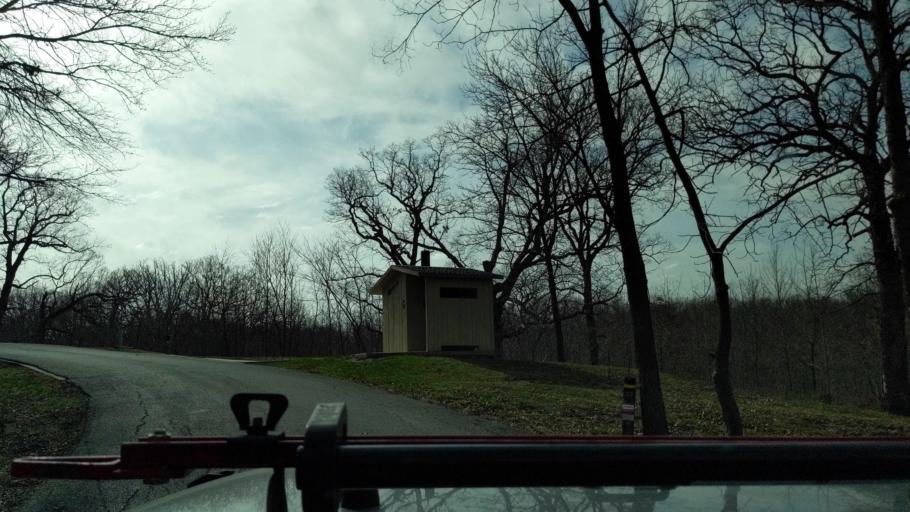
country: US
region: Missouri
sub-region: Macon County
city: Macon
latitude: 39.7727
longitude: -92.5229
